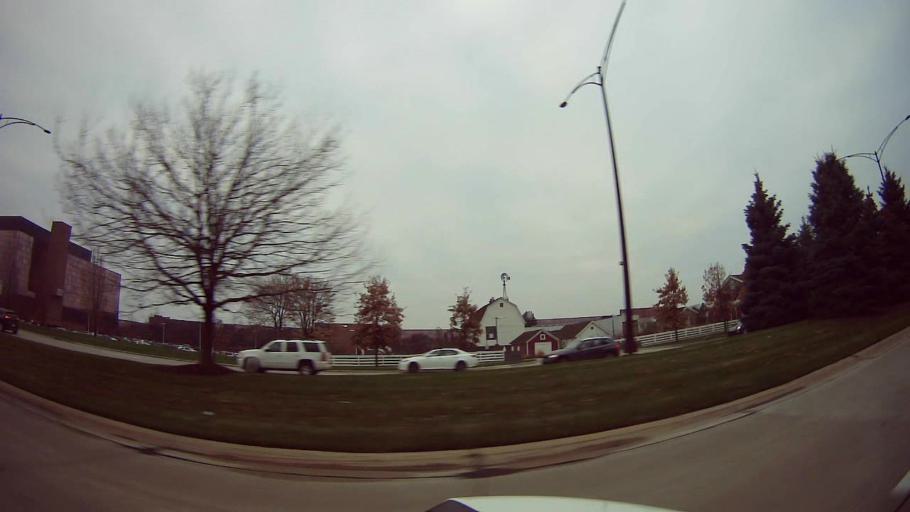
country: US
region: Michigan
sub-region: Oakland County
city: Birmingham
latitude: 42.5613
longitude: -83.1906
